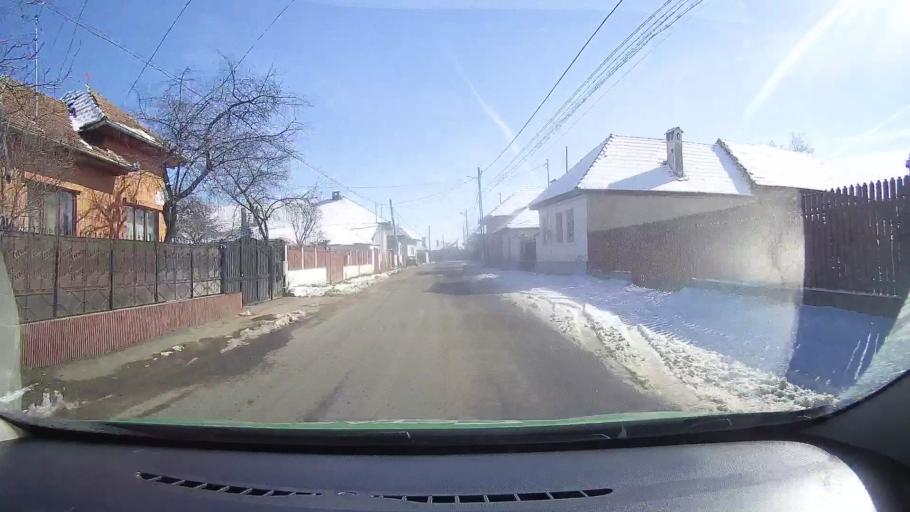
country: RO
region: Brasov
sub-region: Comuna Recea
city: Recea
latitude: 45.7317
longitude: 24.9451
